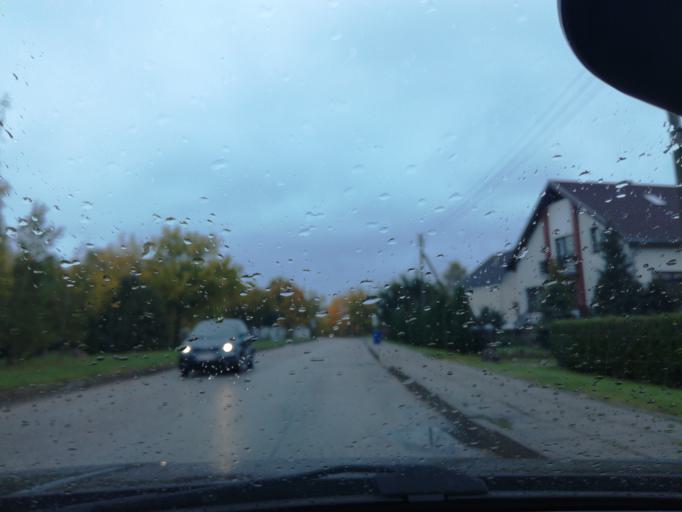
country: LT
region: Alytaus apskritis
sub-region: Alytus
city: Alytus
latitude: 54.4062
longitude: 24.0593
